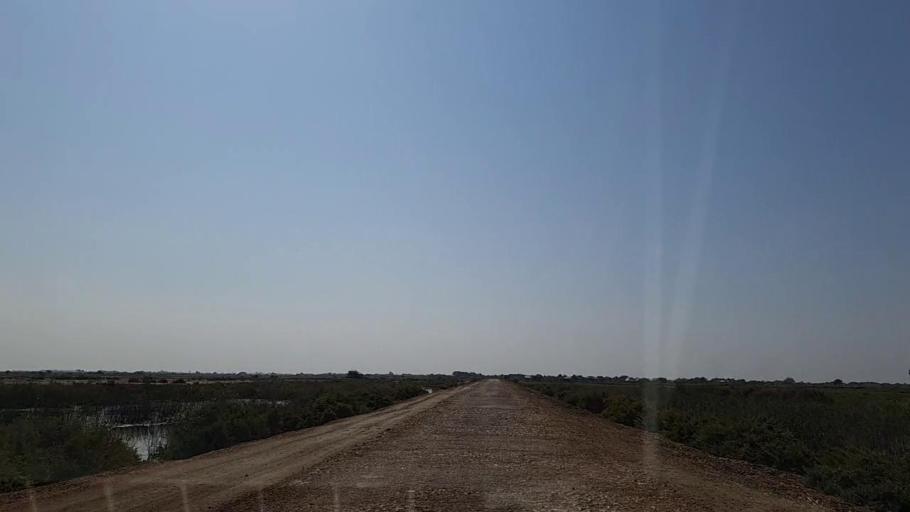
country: PK
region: Sindh
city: Chuhar Jamali
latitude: 24.4777
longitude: 68.0914
